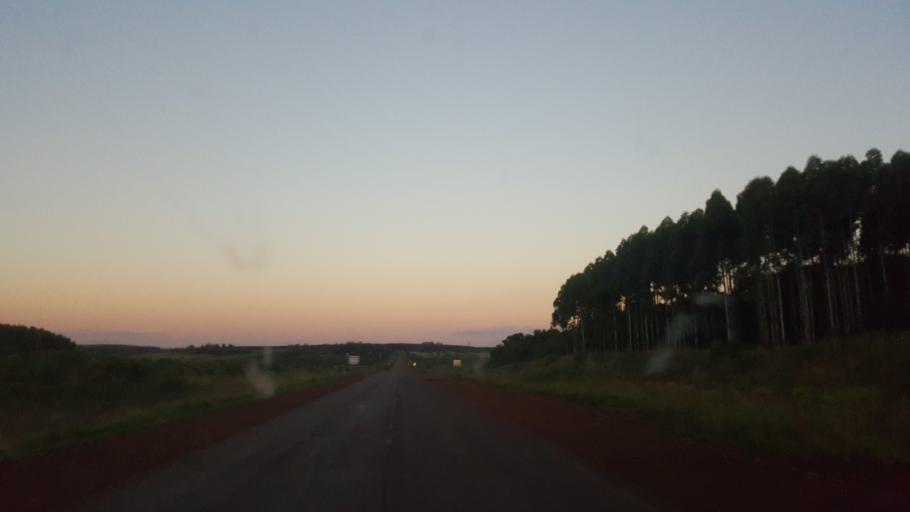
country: AR
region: Corrientes
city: Garruchos
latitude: -28.2379
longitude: -55.8233
